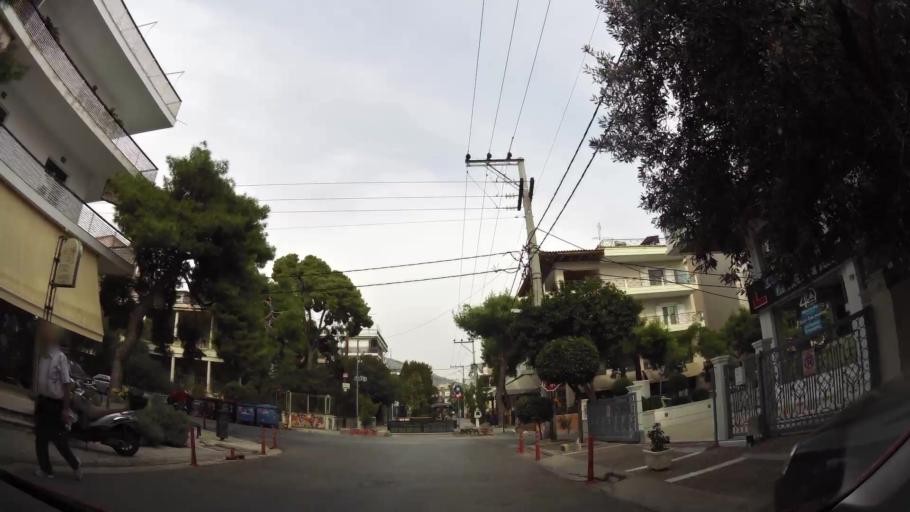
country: GR
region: Attica
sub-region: Nomarchia Athinas
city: Chaidari
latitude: 38.0151
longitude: 23.6501
